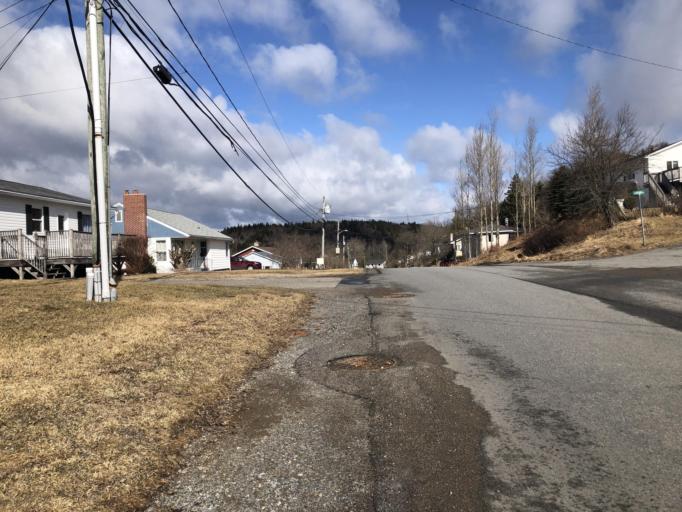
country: CA
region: New Brunswick
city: Saint John
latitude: 45.3195
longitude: -66.0093
